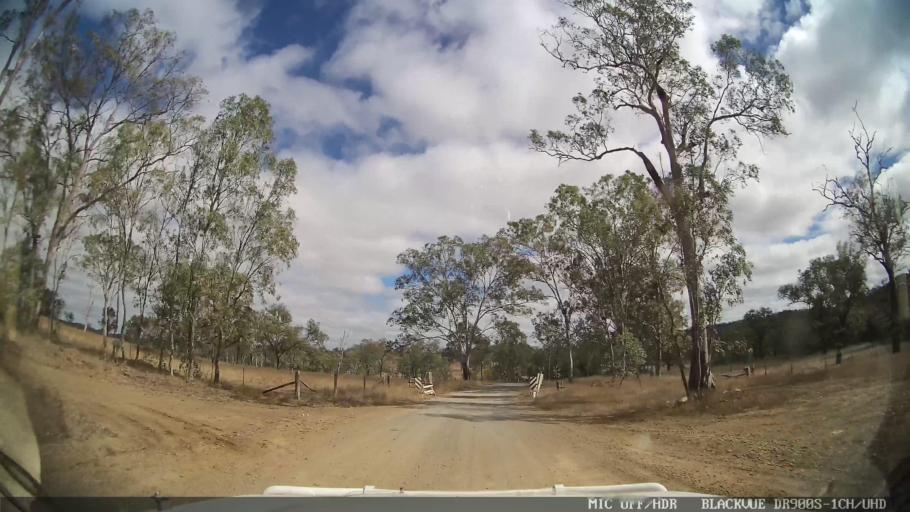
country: AU
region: Queensland
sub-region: Gladstone
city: Toolooa
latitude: -24.6852
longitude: 151.3254
